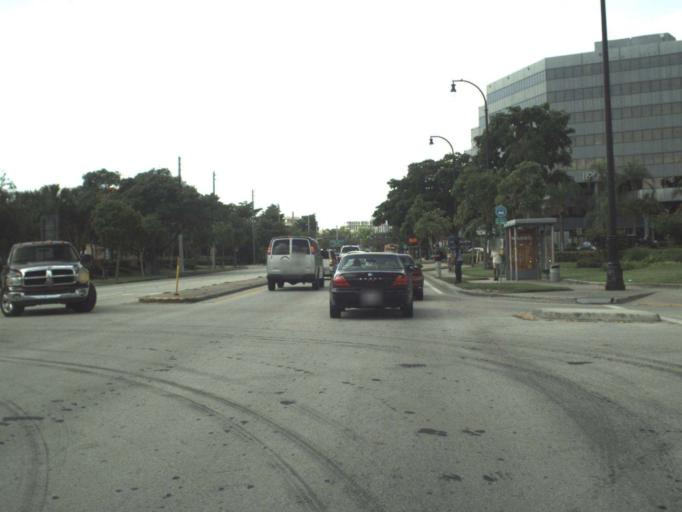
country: US
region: Florida
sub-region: Miami-Dade County
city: Biscayne Park
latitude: 25.8877
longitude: -80.1644
